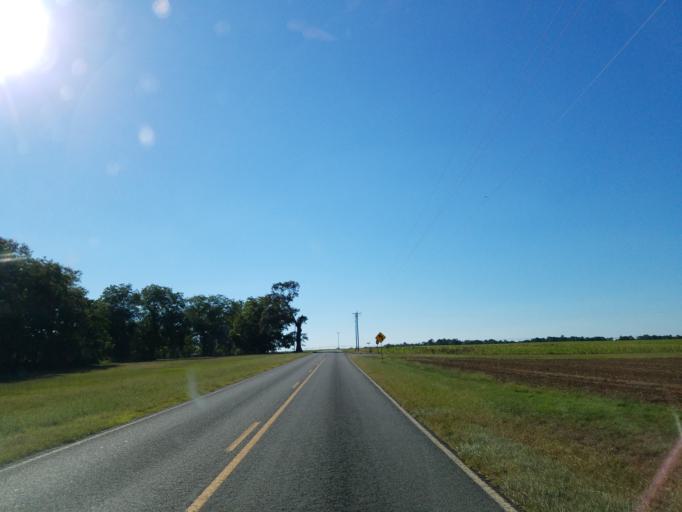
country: US
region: Georgia
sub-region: Dooly County
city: Unadilla
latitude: 32.2446
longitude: -83.8197
